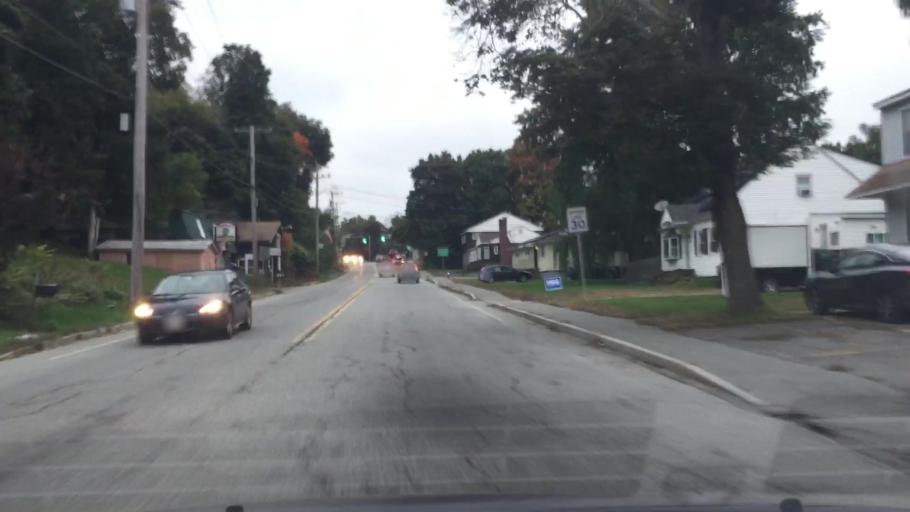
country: US
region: Massachusetts
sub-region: Middlesex County
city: Dracut
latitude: 42.6667
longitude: -71.3033
